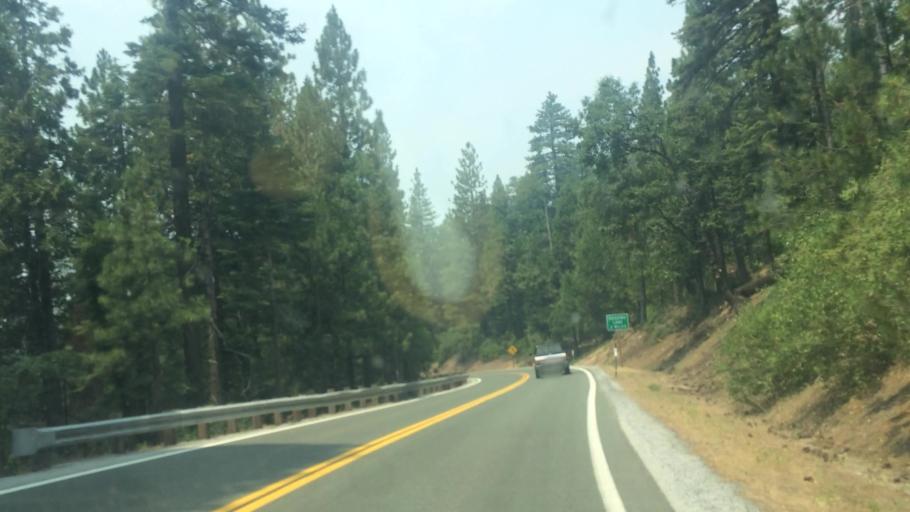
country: US
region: California
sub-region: Amador County
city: Pioneer
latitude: 38.5391
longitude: -120.3860
